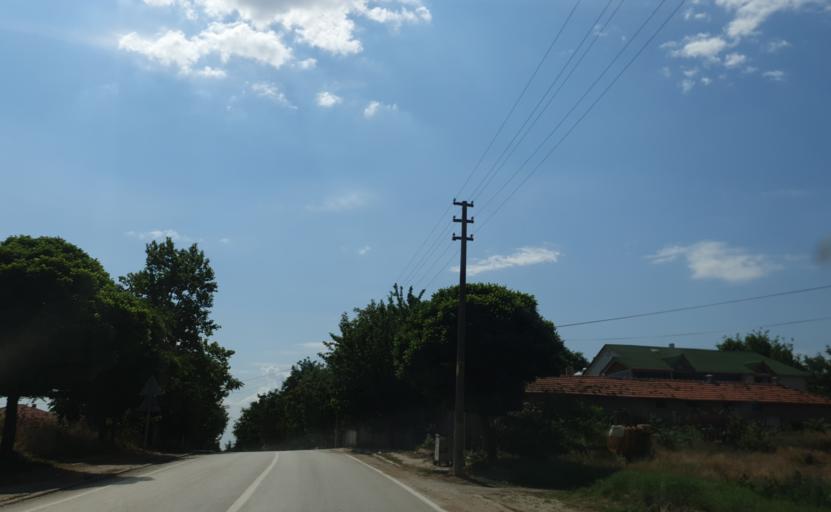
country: TR
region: Tekirdag
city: Beyazkoy
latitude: 41.4434
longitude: 27.5899
